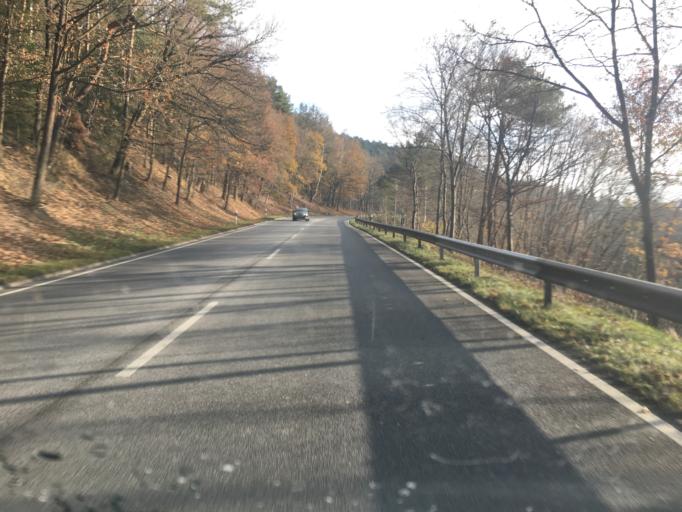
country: DE
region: North Rhine-Westphalia
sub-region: Regierungsbezirk Koln
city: Kall
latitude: 50.5601
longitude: 6.5384
